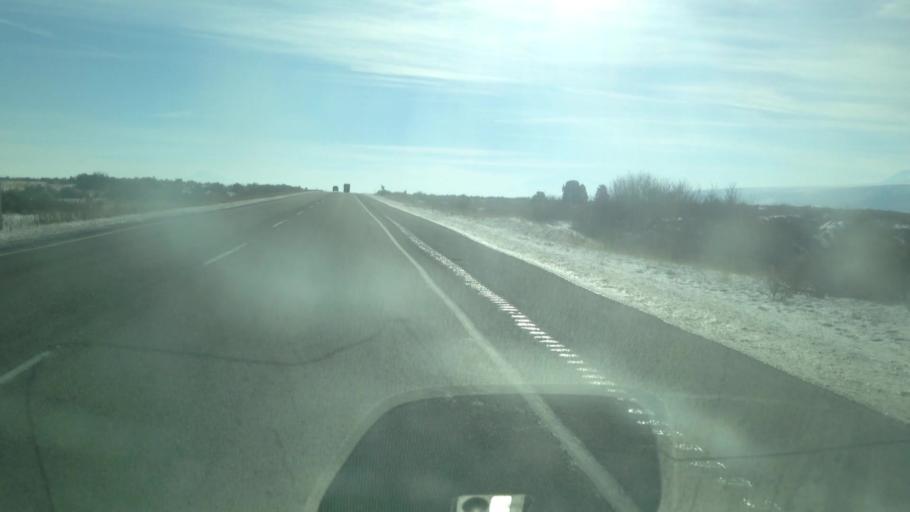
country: US
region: Idaho
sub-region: Bannock County
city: Pocatello
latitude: 42.7182
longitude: -112.2237
